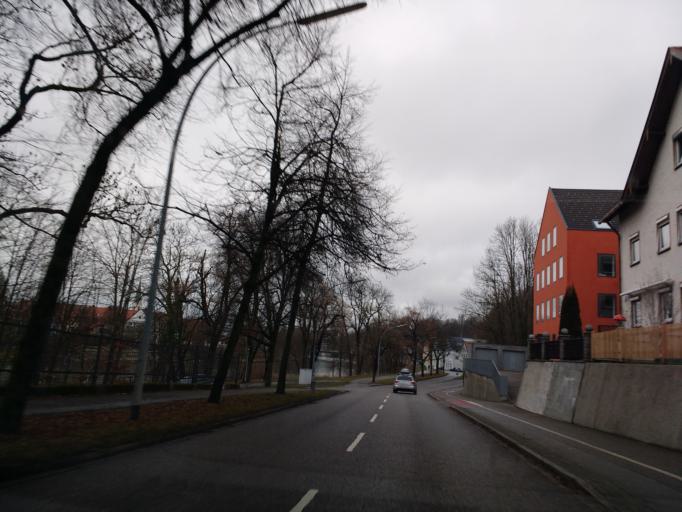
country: DE
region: Bavaria
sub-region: Swabia
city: Kempten (Allgaeu)
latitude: 47.7214
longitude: 10.3252
